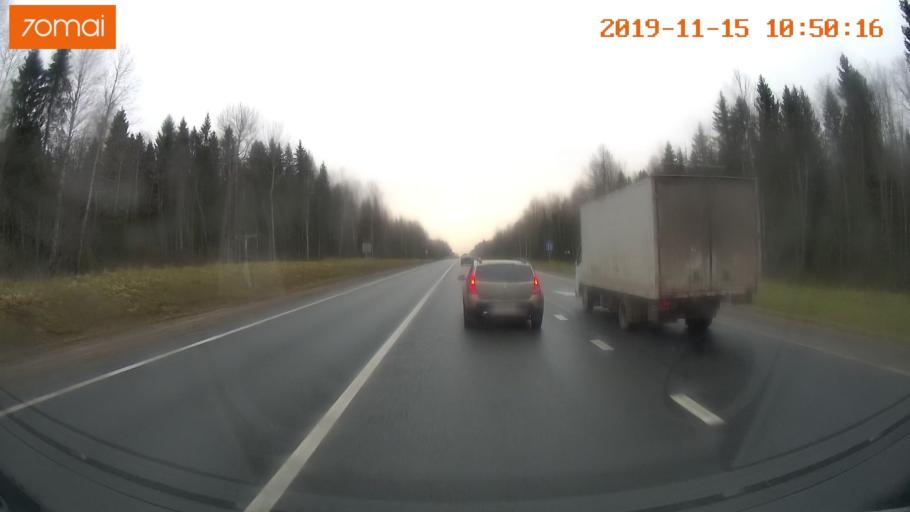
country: RU
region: Vologda
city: Chebsara
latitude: 59.1862
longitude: 38.6776
